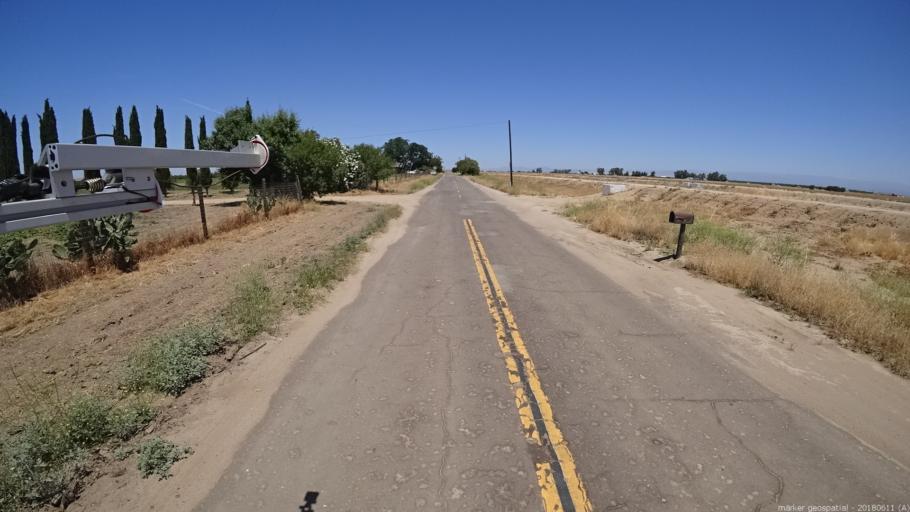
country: US
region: California
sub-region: Madera County
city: Fairmead
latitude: 37.0553
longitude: -120.1844
